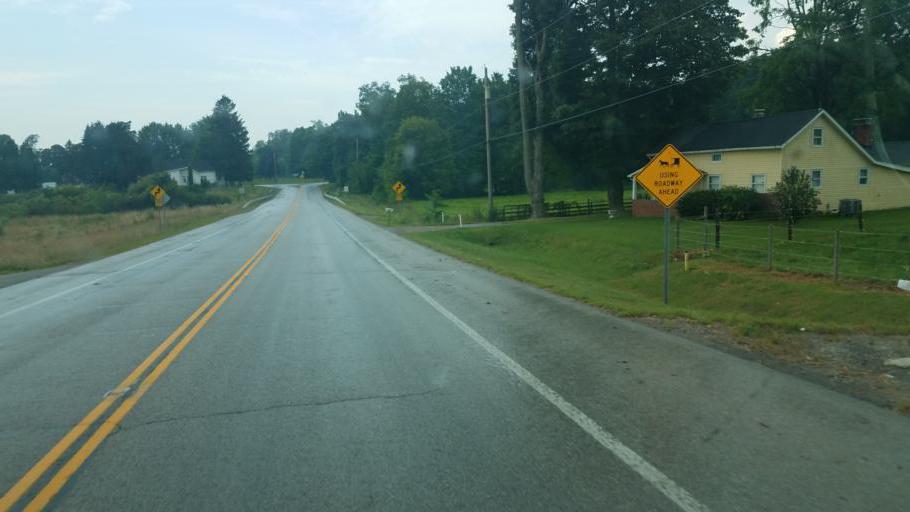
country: US
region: Ohio
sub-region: Ashtabula County
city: Orwell
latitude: 41.4652
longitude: -80.9540
